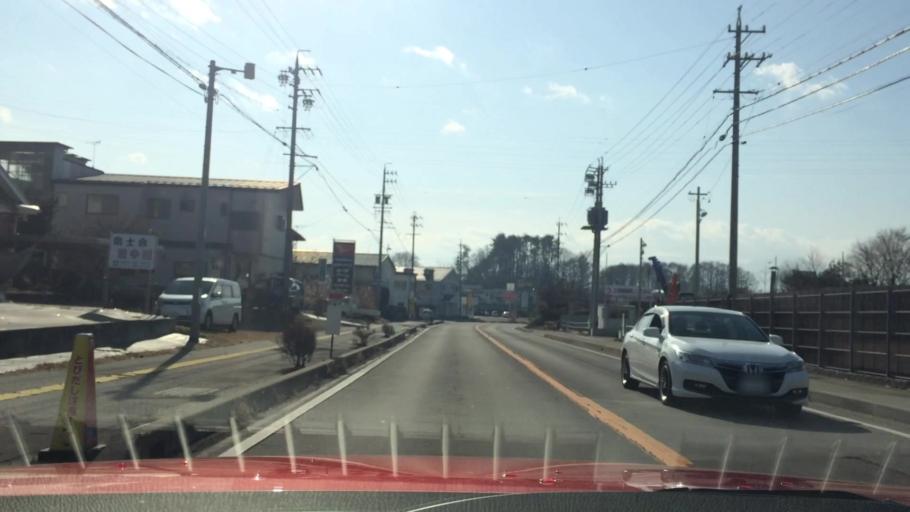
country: JP
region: Nagano
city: Komoro
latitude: 36.2926
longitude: 138.4912
